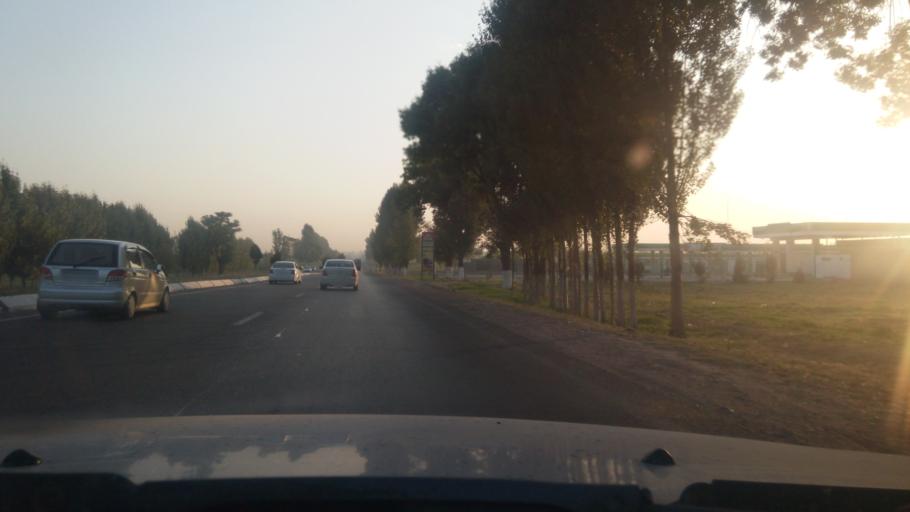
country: UZ
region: Toshkent
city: Urtaowul
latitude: 41.1797
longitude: 69.0782
